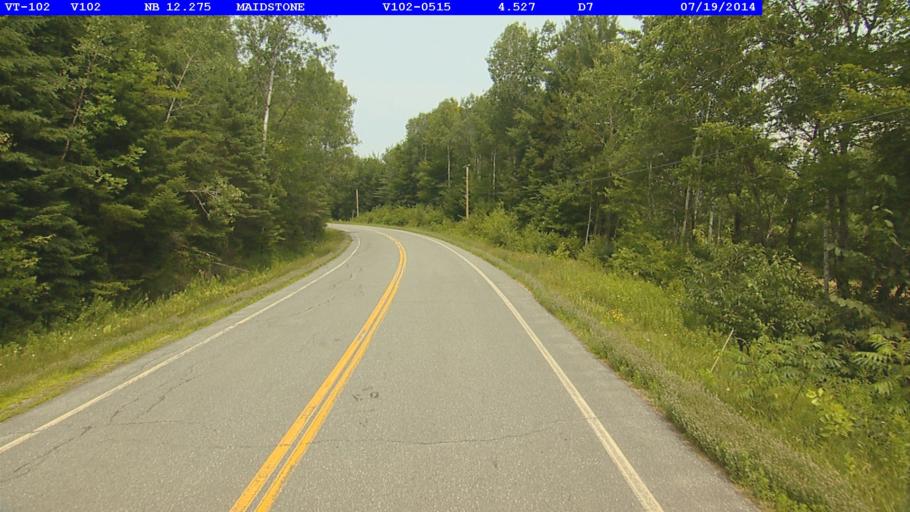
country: US
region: New Hampshire
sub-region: Coos County
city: Stratford
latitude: 44.6254
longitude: -71.5559
